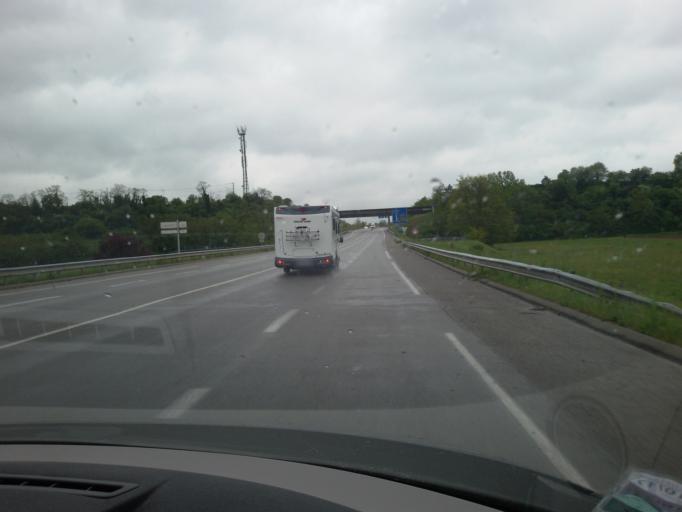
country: FR
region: Rhone-Alpes
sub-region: Departement de la Drome
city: Bourg-de-Peage
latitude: 45.0295
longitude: 5.0801
